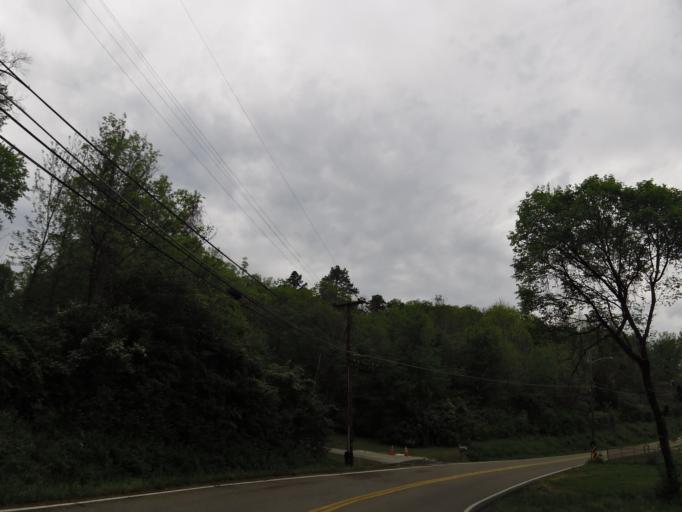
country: US
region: Tennessee
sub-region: Knox County
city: Knoxville
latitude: 36.0219
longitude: -83.9204
